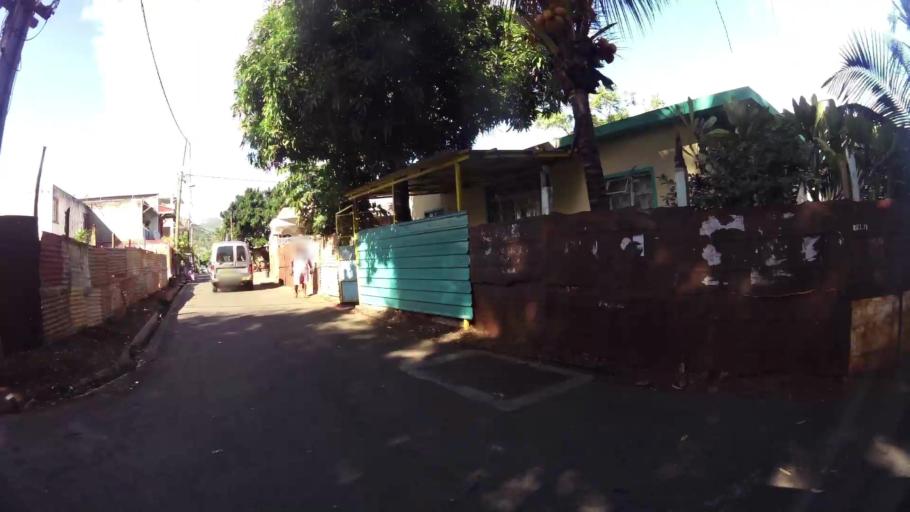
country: MU
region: Pamplemousses
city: Le Hochet
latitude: -20.1437
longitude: 57.5173
